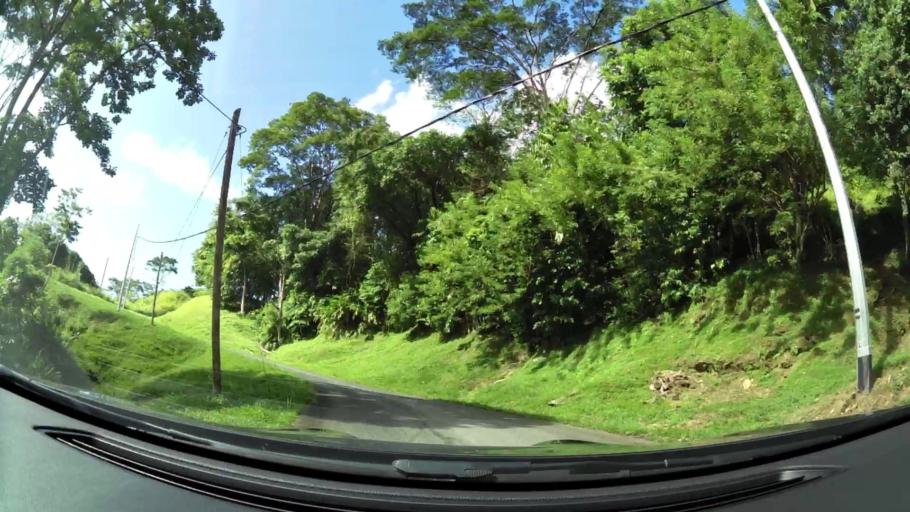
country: TT
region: Eastern Tobago
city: Roxborough
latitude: 11.3061
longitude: -60.6276
